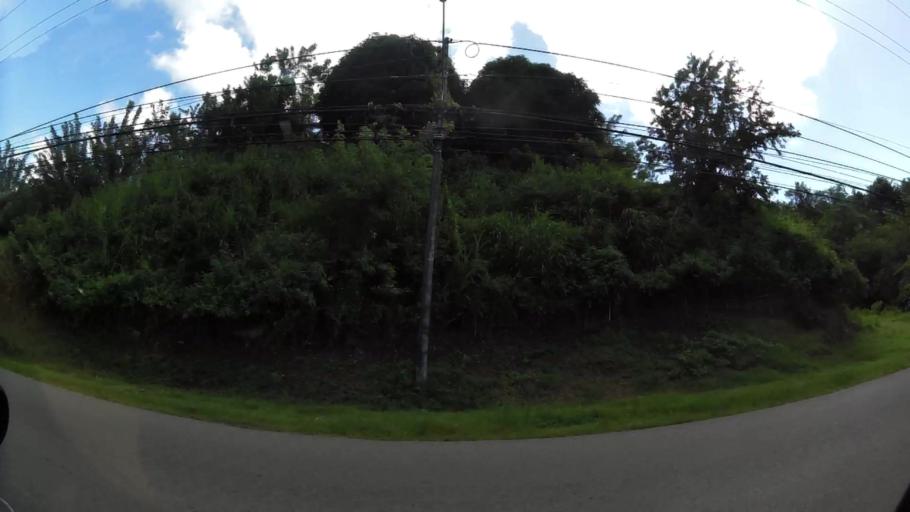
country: TT
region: Tobago
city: Scarborough
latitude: 11.2041
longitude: -60.7819
